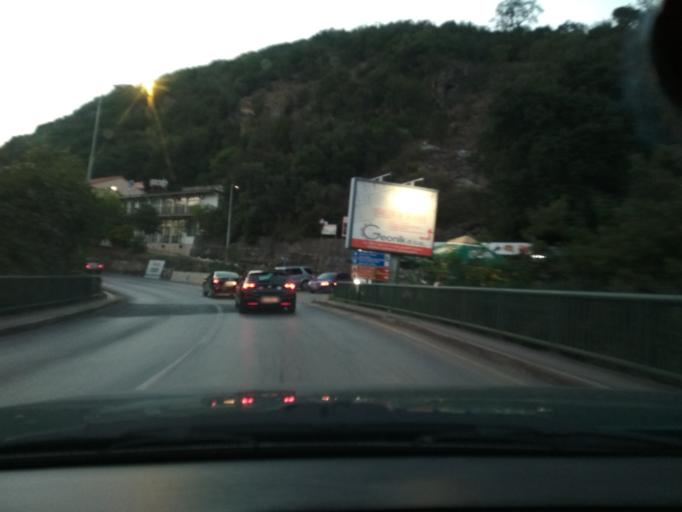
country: ME
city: Igalo
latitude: 42.4619
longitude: 18.5202
